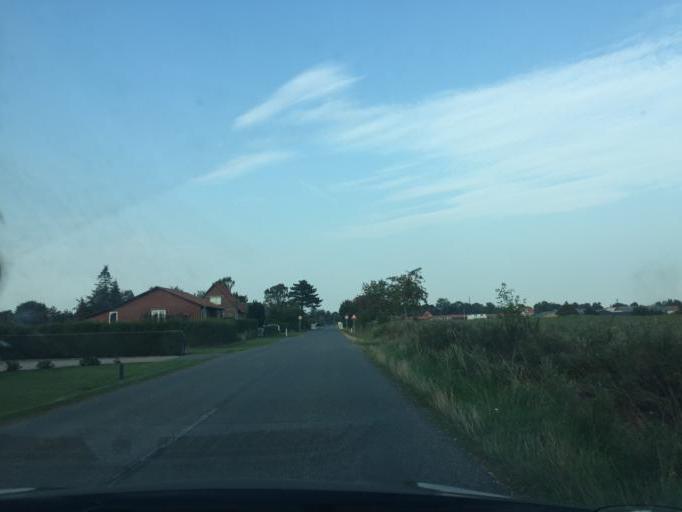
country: DK
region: South Denmark
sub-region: Kerteminde Kommune
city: Langeskov
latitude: 55.3045
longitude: 10.5811
